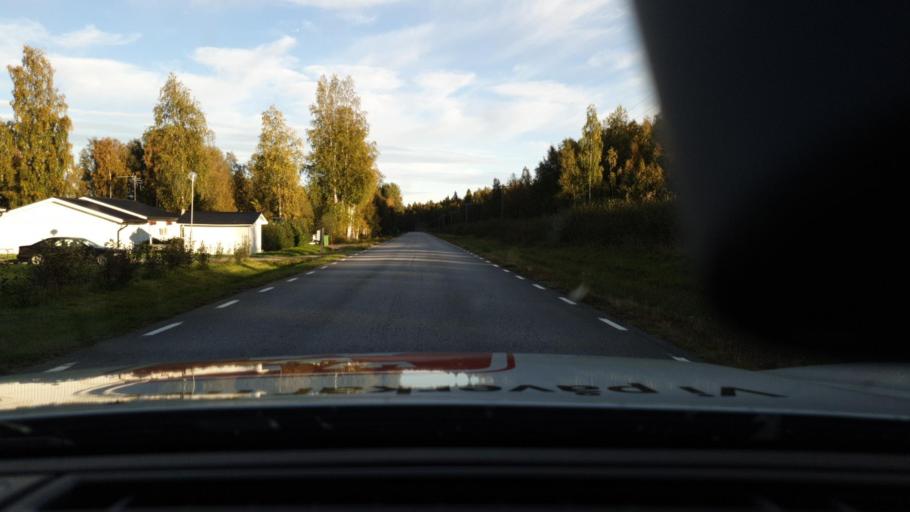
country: SE
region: Norrbotten
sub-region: Kalix Kommun
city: Toere
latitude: 65.8927
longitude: 22.6383
